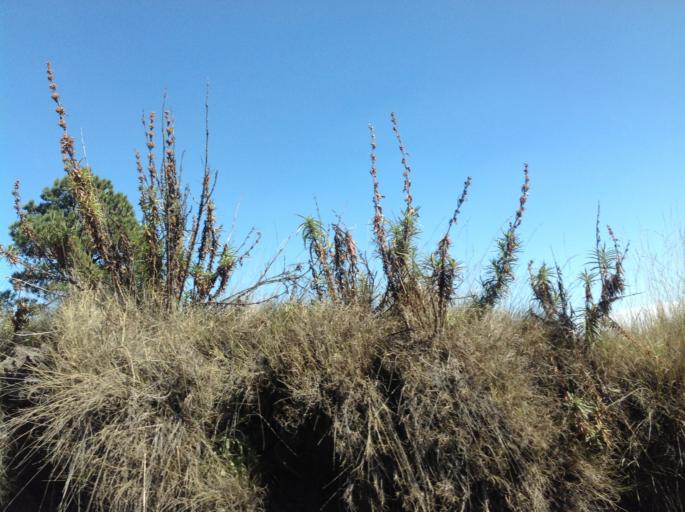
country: MX
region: Mexico
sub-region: Amecameca
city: San Diego Huehuecalco
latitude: 19.1070
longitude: -98.6454
